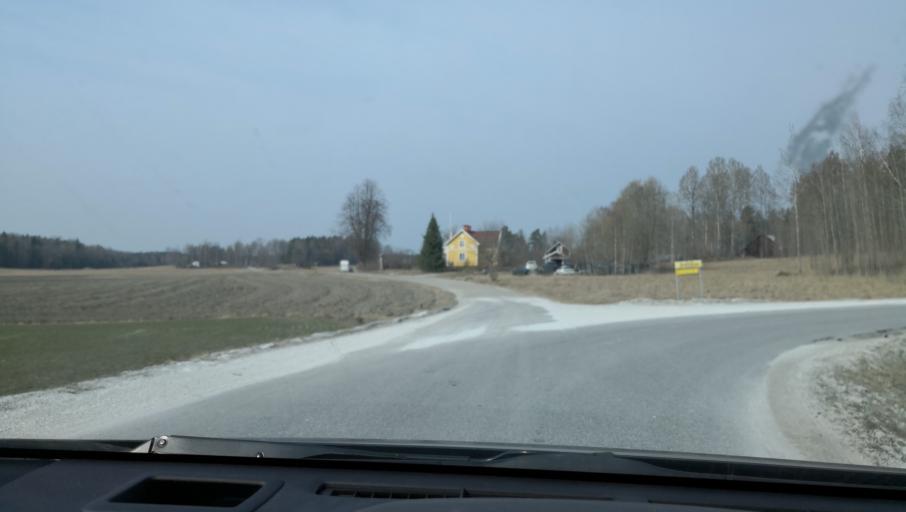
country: SE
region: OErebro
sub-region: Lindesbergs Kommun
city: Frovi
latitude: 59.3441
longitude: 15.4467
